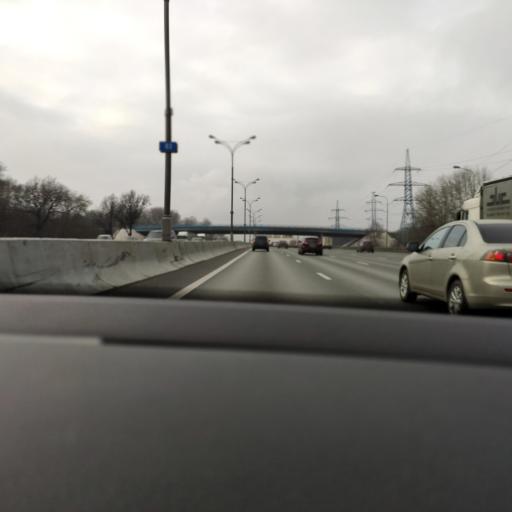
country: RU
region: Moscow
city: Lianozovo
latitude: 55.9098
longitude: 37.5691
